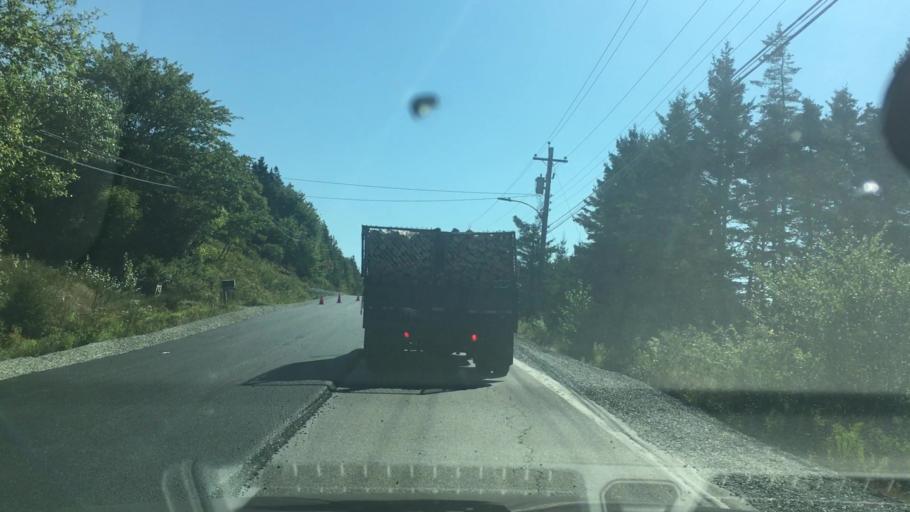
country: CA
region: Nova Scotia
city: New Glasgow
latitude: 44.9106
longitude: -62.5053
